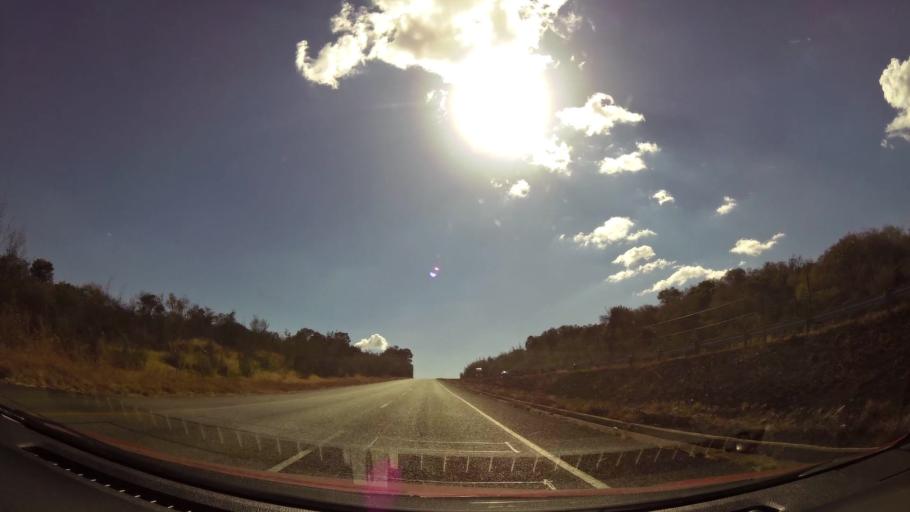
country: ZA
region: North-West
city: Fochville
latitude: -26.4254
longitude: 27.4630
